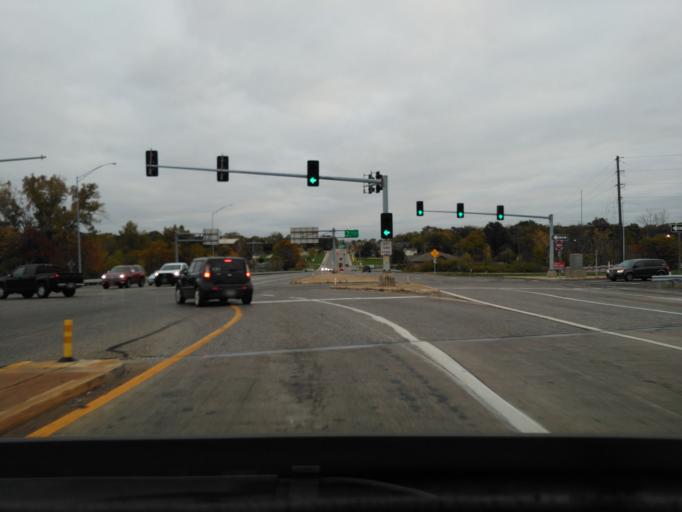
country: US
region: Missouri
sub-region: Saint Louis County
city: Concord
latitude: 38.5133
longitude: -90.3710
